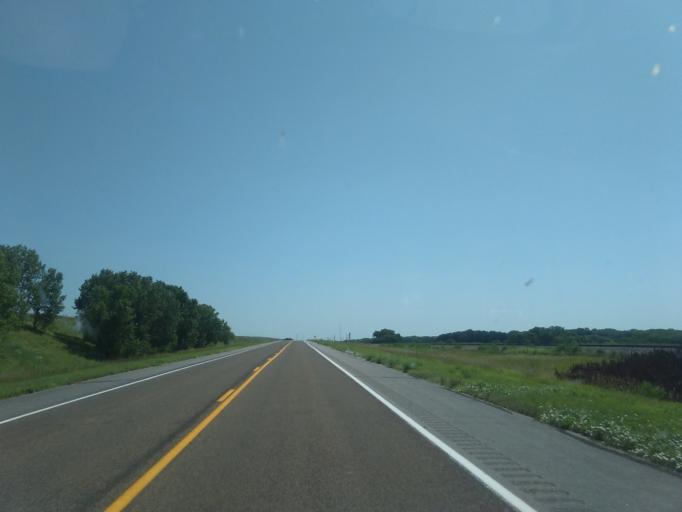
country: US
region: Nebraska
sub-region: Hitchcock County
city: Trenton
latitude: 40.1595
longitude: -101.1679
